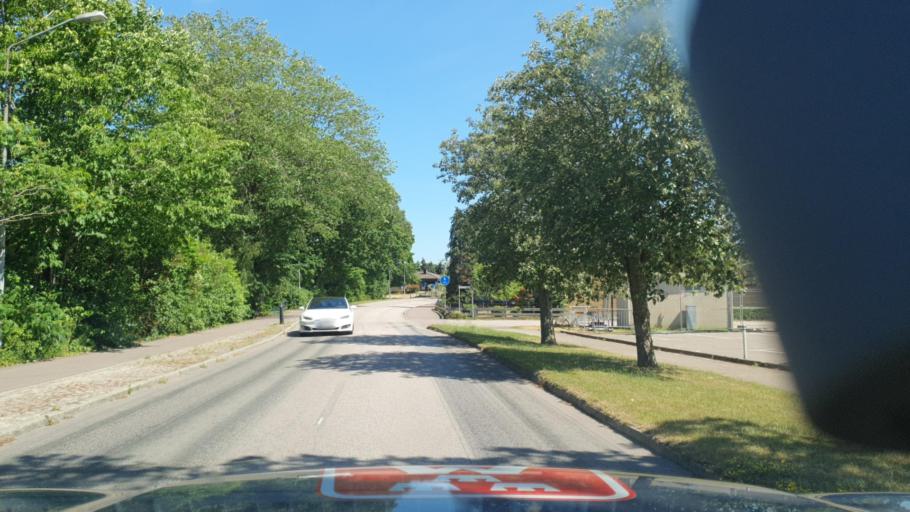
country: SE
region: Kalmar
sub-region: Torsas Kommun
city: Torsas
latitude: 56.3919
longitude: 16.0752
